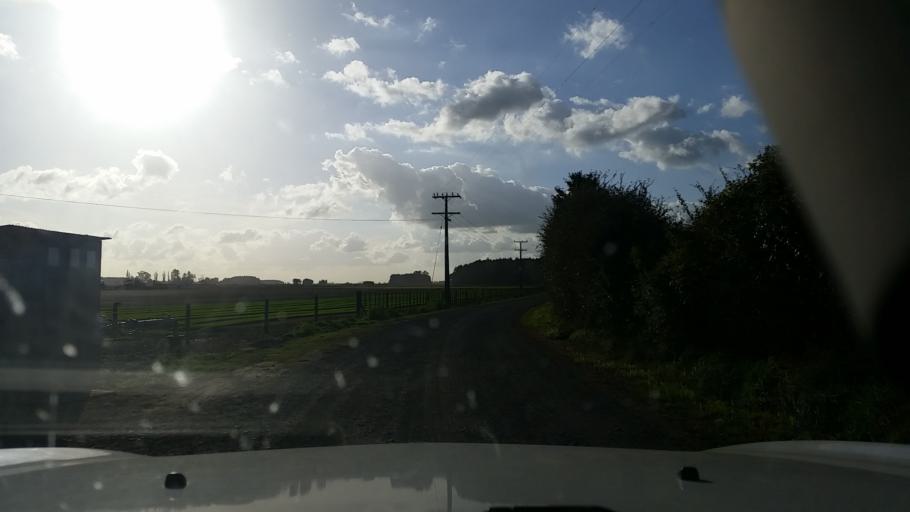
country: NZ
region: Waikato
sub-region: Matamata-Piako District
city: Matamata
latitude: -37.7383
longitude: 175.7548
